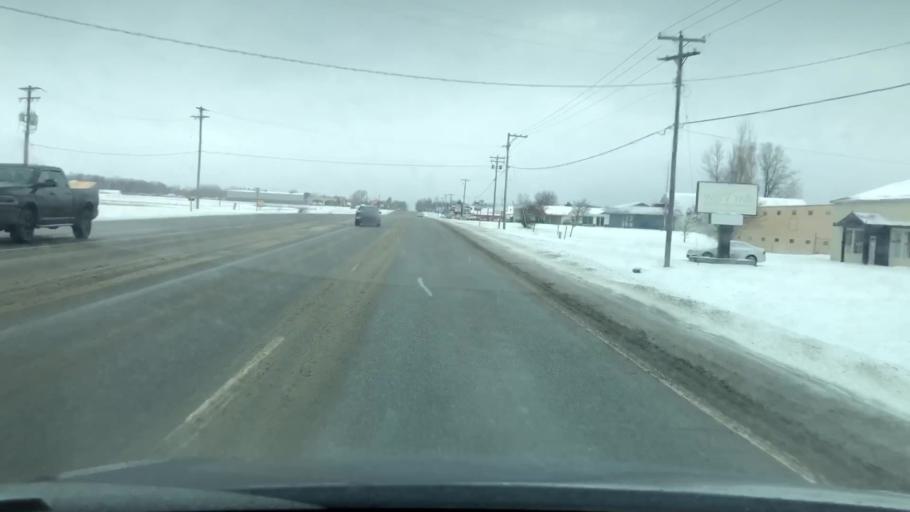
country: US
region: Michigan
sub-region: Grand Traverse County
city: Traverse City
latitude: 44.6904
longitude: -85.6562
